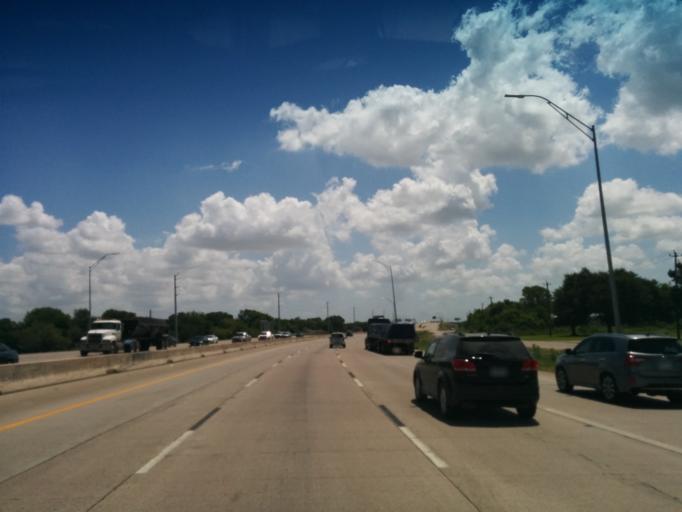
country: US
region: Texas
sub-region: Harris County
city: Highlands
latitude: 29.7994
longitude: -95.0266
